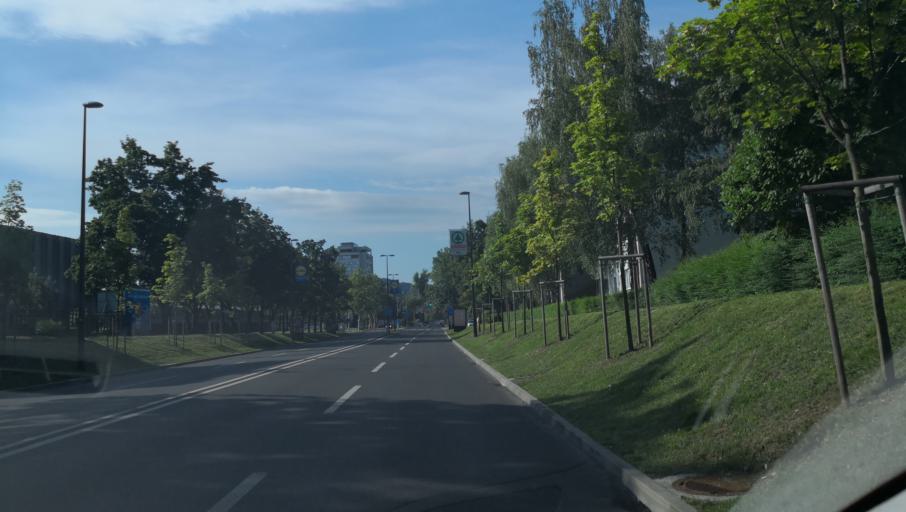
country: SI
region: Ljubljana
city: Ljubljana
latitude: 46.0586
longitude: 14.5402
